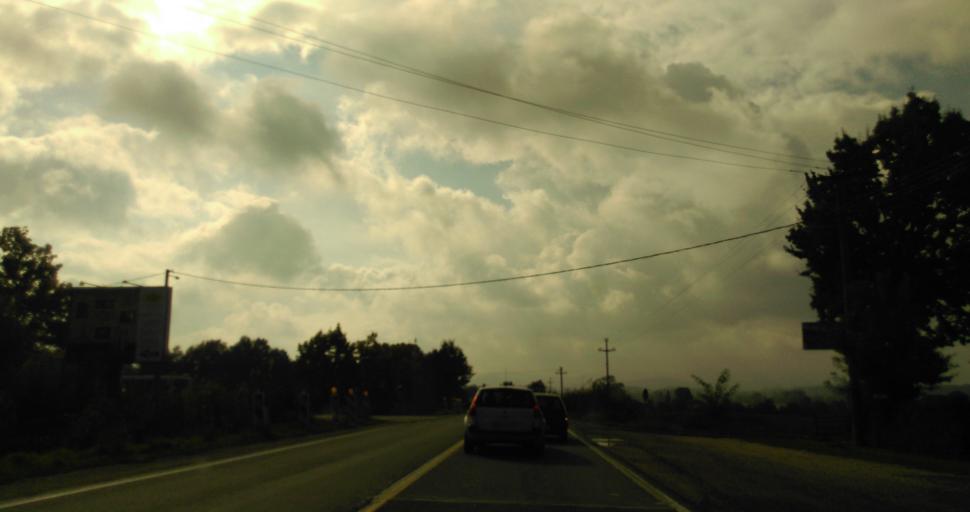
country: RS
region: Central Serbia
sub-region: Kolubarski Okrug
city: Ljig
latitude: 44.3002
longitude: 20.2598
